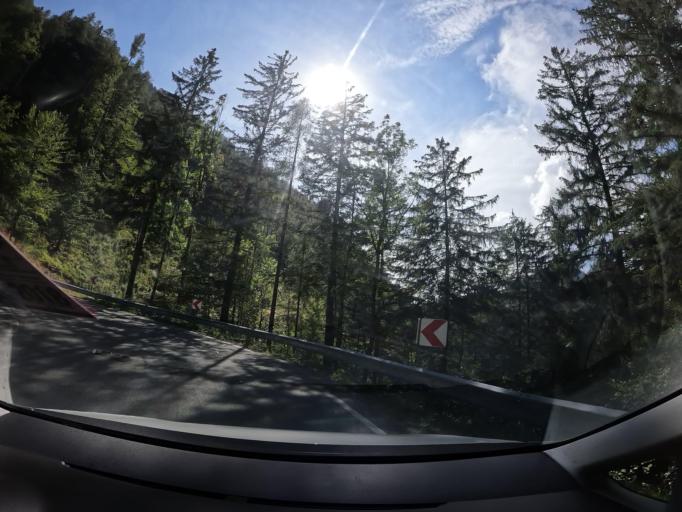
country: AT
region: Carinthia
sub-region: Politischer Bezirk Villach Land
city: Sankt Jakob
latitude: 46.5263
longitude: 14.0938
